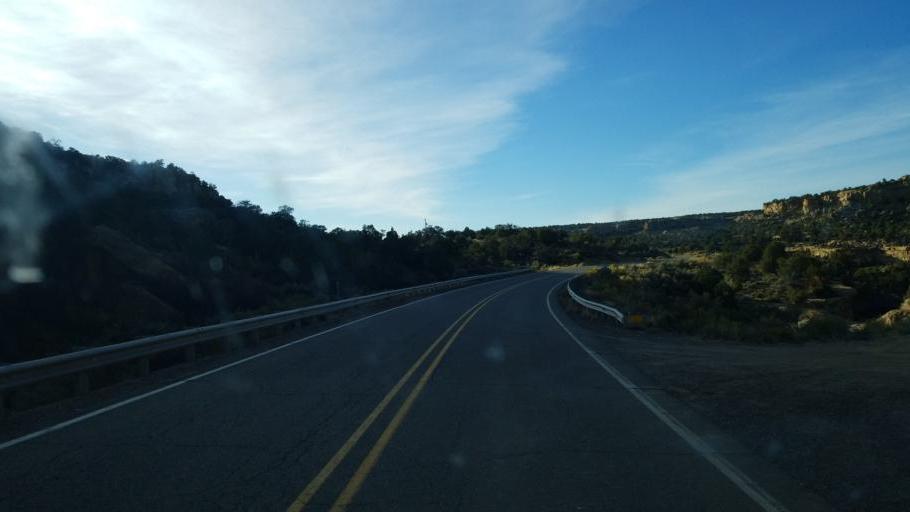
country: US
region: New Mexico
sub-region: San Juan County
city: Bloomfield
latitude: 36.7373
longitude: -107.7077
